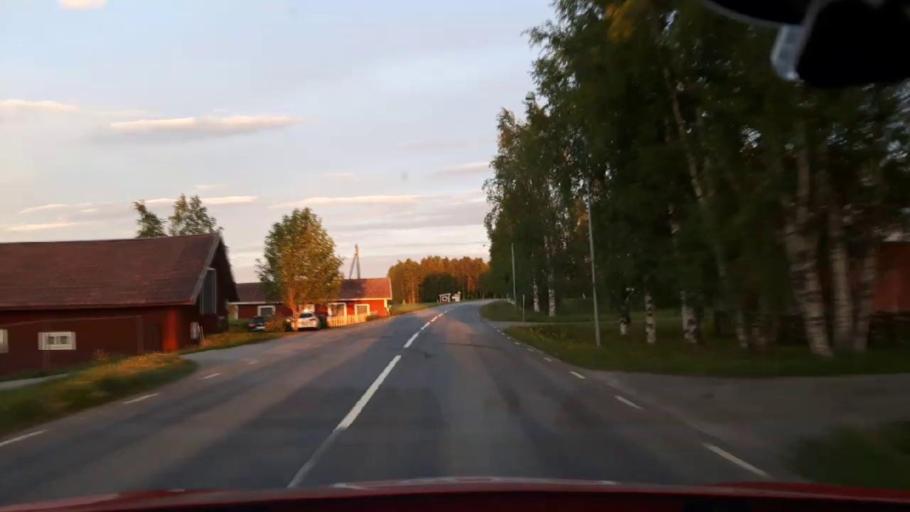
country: SE
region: Jaemtland
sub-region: OEstersunds Kommun
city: Brunflo
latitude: 63.0977
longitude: 14.7439
